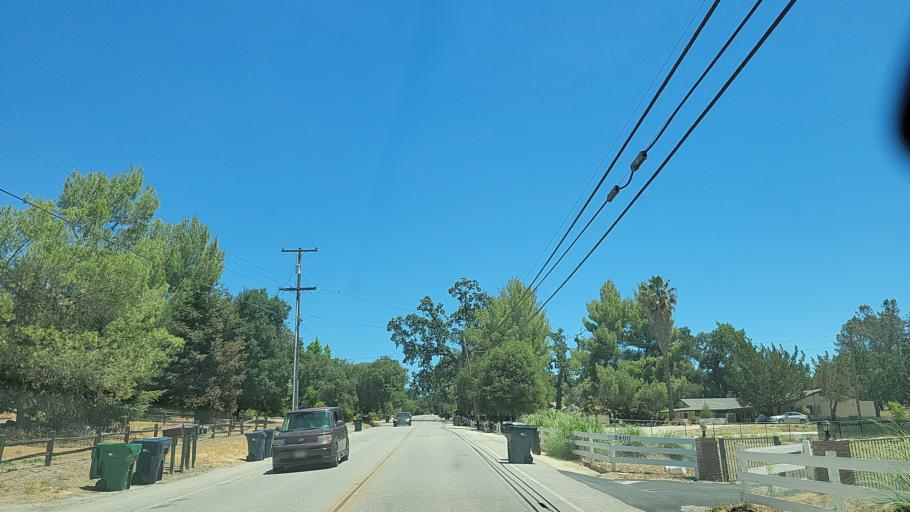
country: US
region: California
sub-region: San Luis Obispo County
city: Atascadero
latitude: 35.4708
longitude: -120.6625
